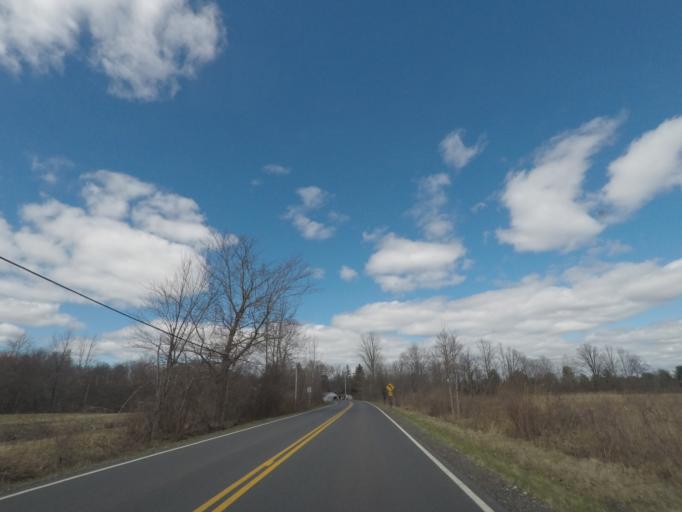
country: US
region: New York
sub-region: Albany County
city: Delmar
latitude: 42.5707
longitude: -73.8254
